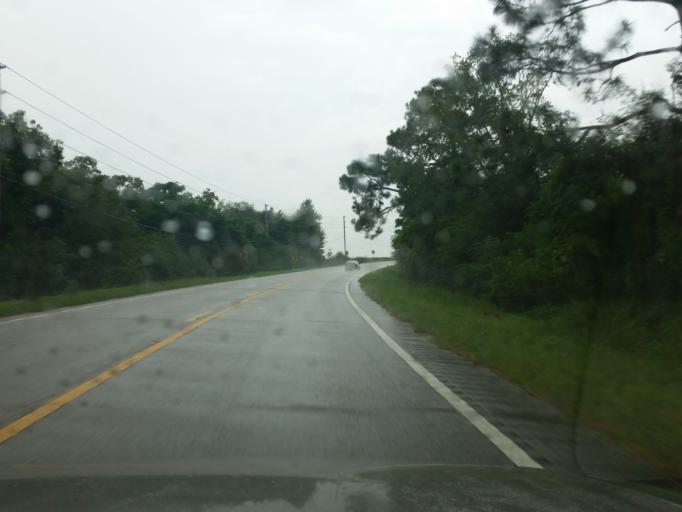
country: US
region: Alabama
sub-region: Baldwin County
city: Elberta
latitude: 30.5388
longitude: -87.5592
